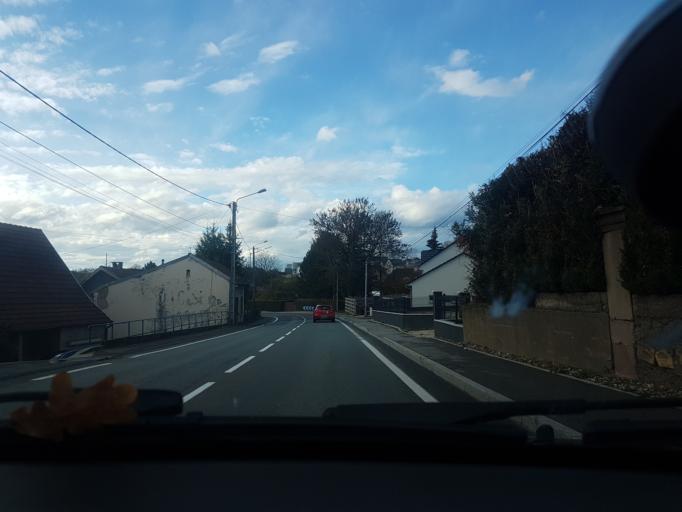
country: FR
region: Franche-Comte
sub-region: Territoire de Belfort
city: Essert
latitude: 47.6345
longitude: 6.8127
